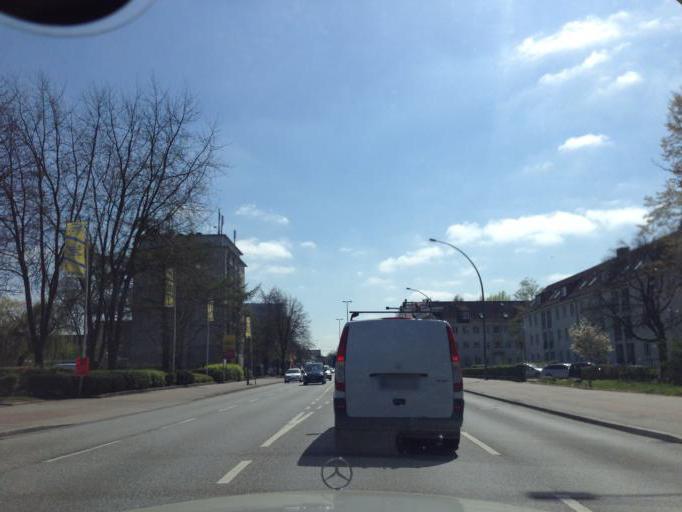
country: DE
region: Hamburg
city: Wandsbek
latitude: 53.5816
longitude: 10.1018
